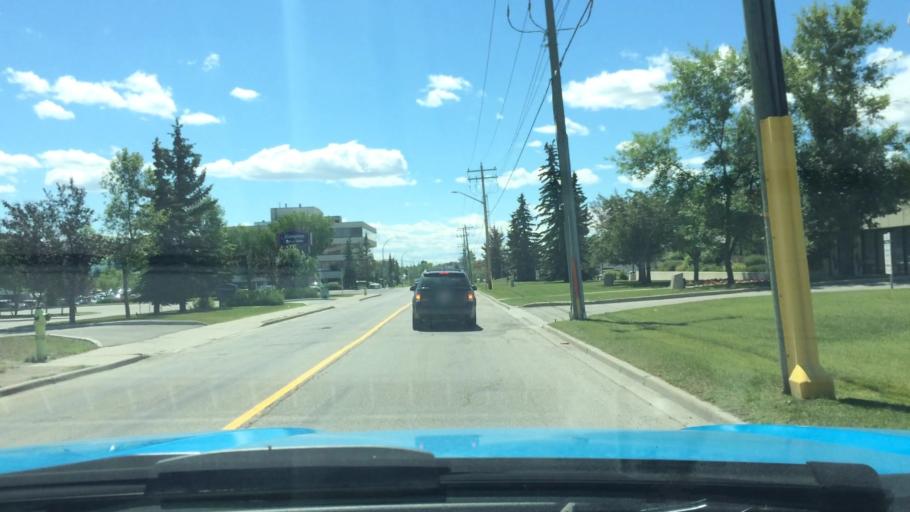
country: CA
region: Alberta
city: Calgary
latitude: 51.0877
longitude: -114.0051
